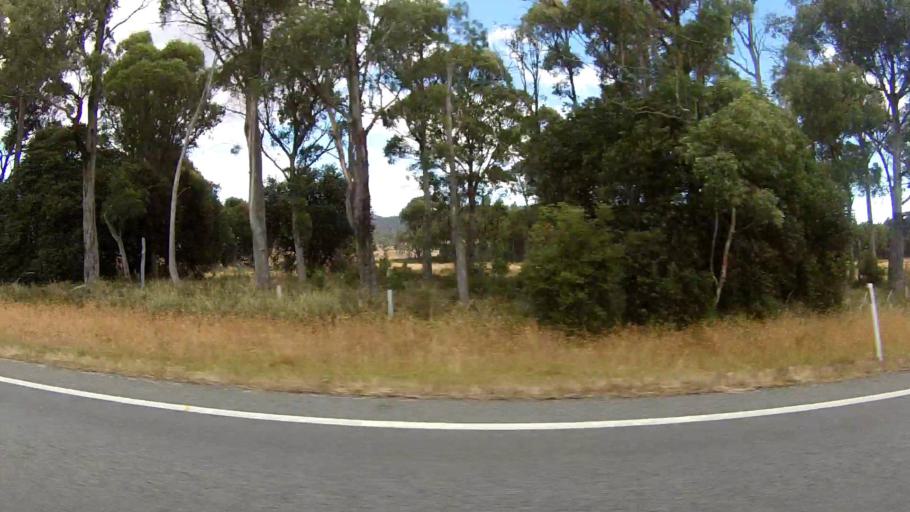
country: AU
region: Tasmania
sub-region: Sorell
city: Sorell
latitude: -42.6370
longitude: 147.5922
